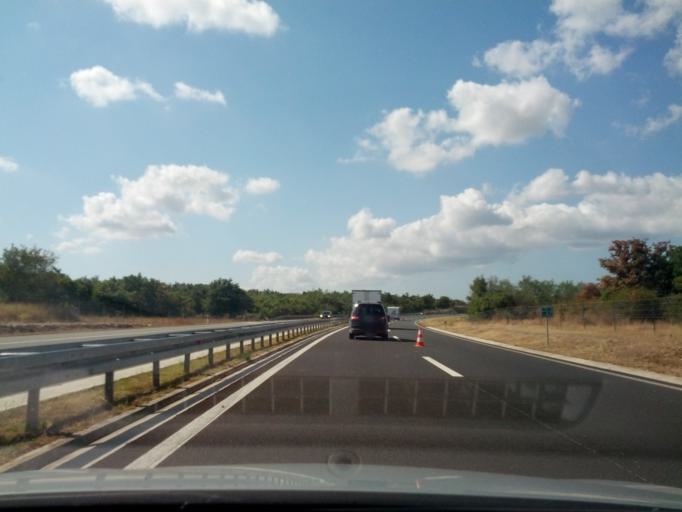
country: HR
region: Istarska
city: Vodnjan
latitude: 45.0210
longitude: 13.8420
